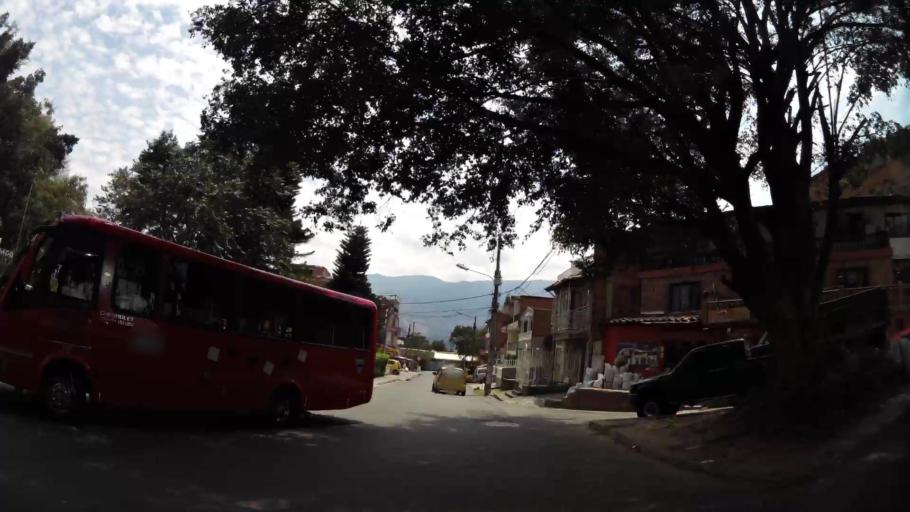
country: CO
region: Antioquia
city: Bello
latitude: 6.3107
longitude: -75.5701
